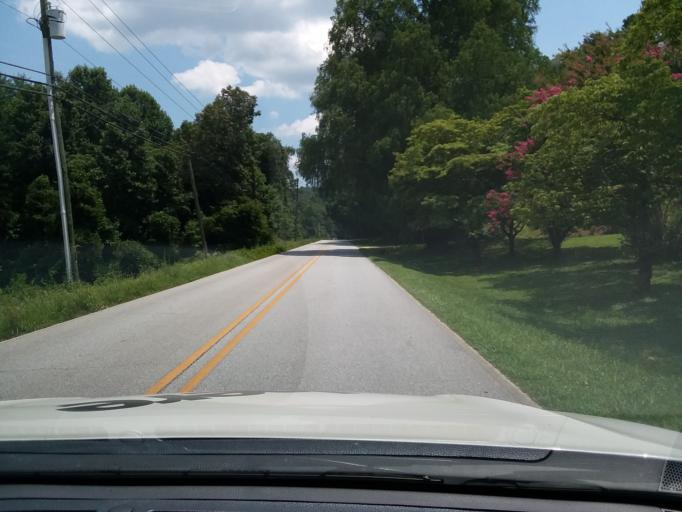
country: US
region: Georgia
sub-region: Rabun County
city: Clayton
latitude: 34.7965
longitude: -83.4185
